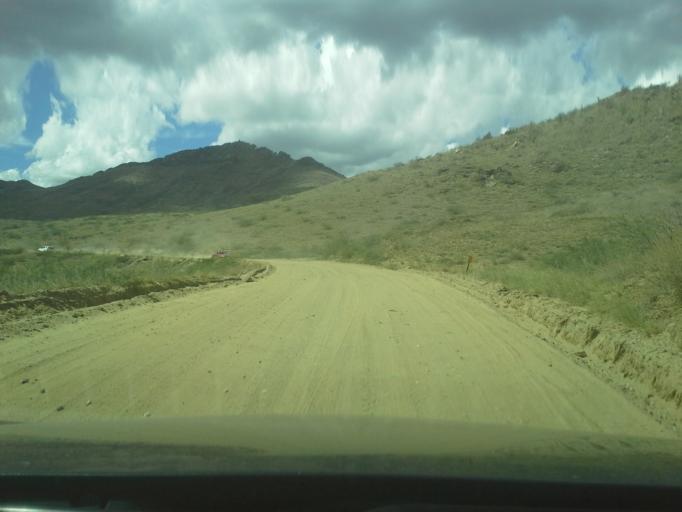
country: US
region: Arizona
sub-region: Yavapai County
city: Spring Valley
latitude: 34.2769
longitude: -112.2478
